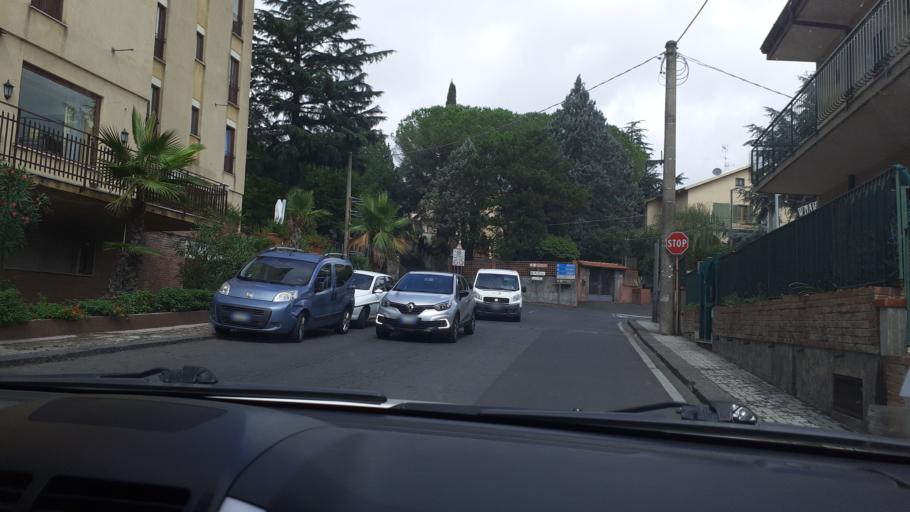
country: IT
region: Sicily
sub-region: Catania
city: Pedara
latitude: 37.6154
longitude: 15.0520
